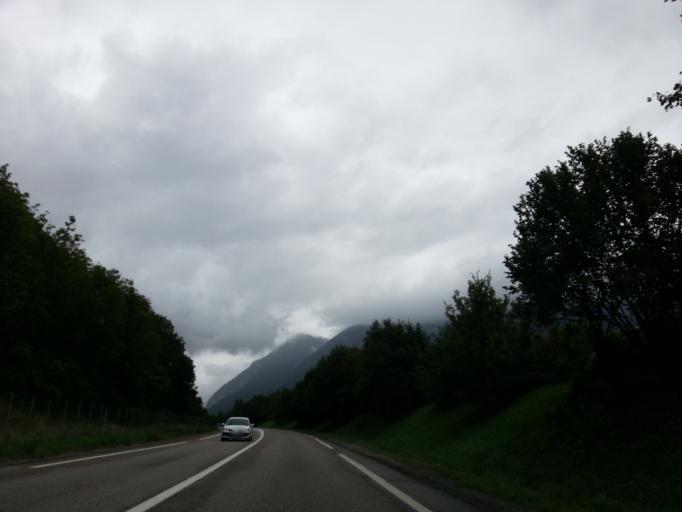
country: FR
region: Rhone-Alpes
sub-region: Departement de la Haute-Savoie
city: Faverges
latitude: 45.7545
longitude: 6.2872
